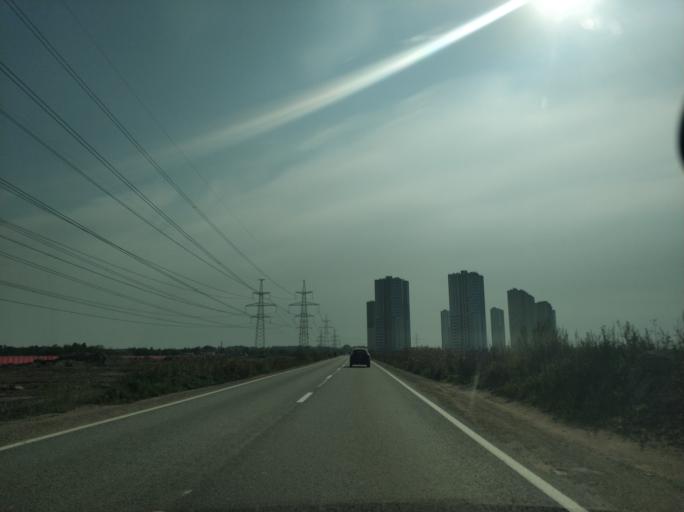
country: RU
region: Leningrad
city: Murino
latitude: 60.0156
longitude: 30.4721
